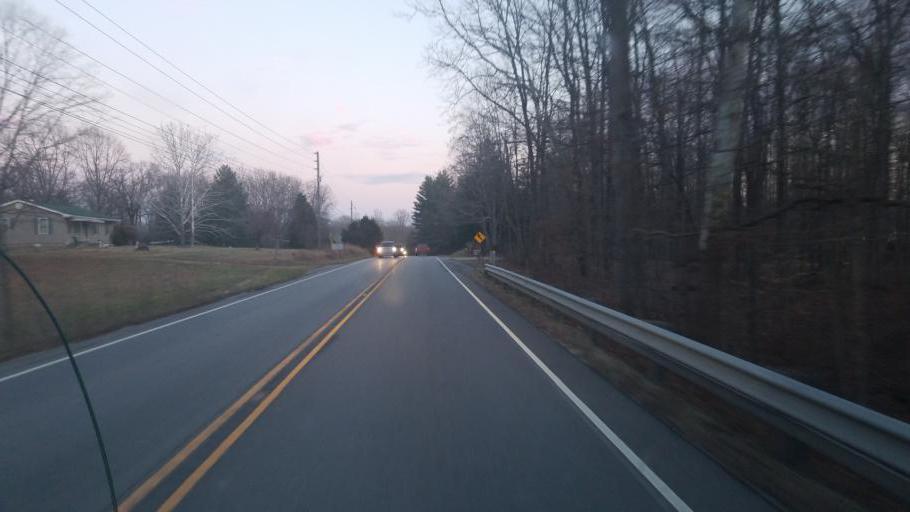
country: US
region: Indiana
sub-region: Jackson County
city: Brownstown
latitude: 38.8847
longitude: -86.2624
